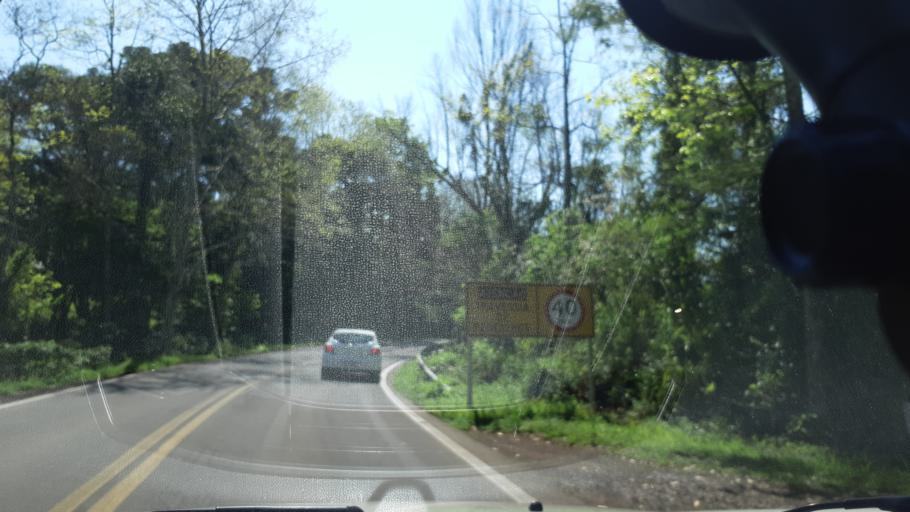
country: BR
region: Rio Grande do Sul
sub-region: Nova Petropolis
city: Nova Petropolis
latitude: -29.3952
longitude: -51.1241
